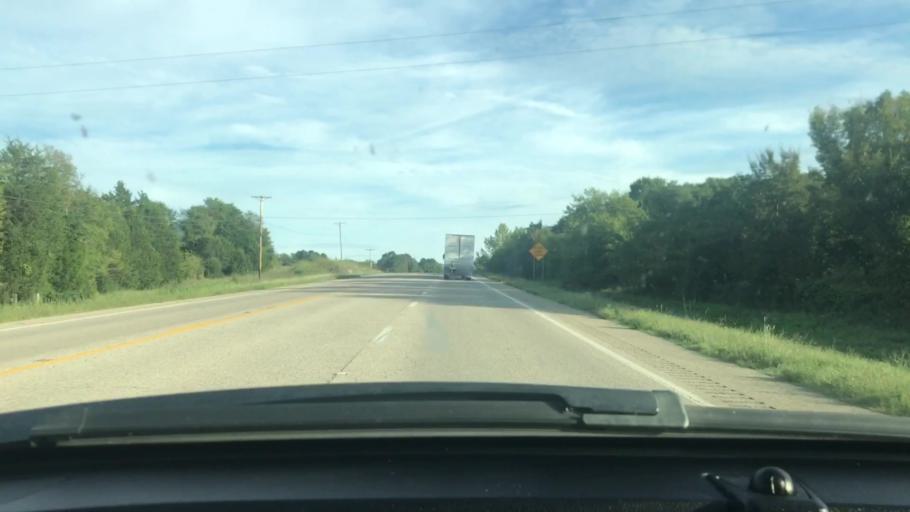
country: US
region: Arkansas
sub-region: Randolph County
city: Pocahontas
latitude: 36.1911
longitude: -91.1648
